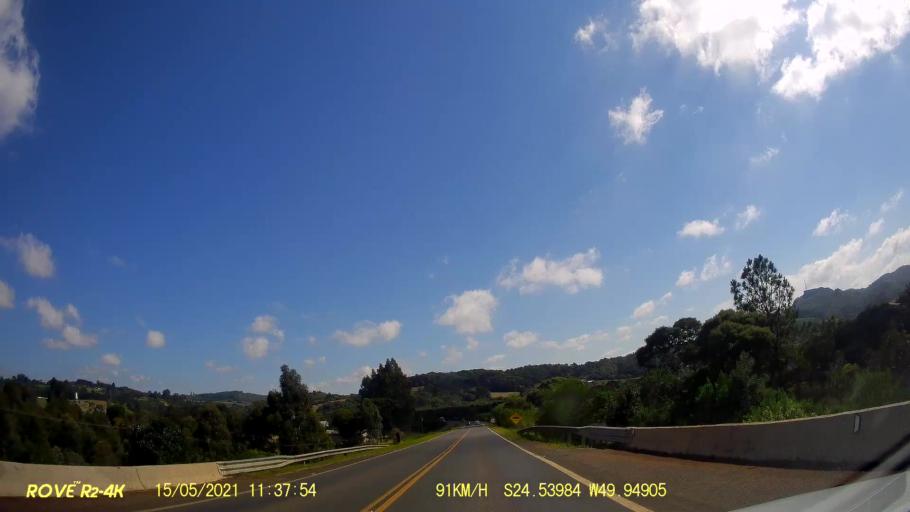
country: BR
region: Parana
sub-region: Pirai Do Sul
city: Pirai do Sul
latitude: -24.5399
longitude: -49.9485
